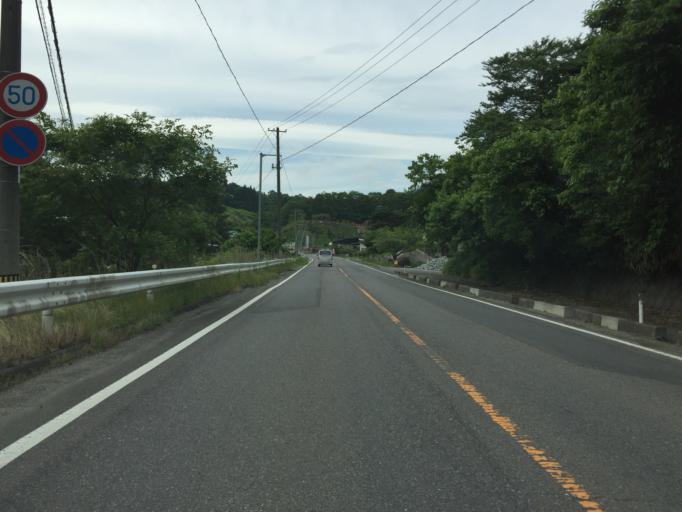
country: JP
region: Fukushima
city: Funehikimachi-funehiki
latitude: 37.4598
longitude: 140.7502
